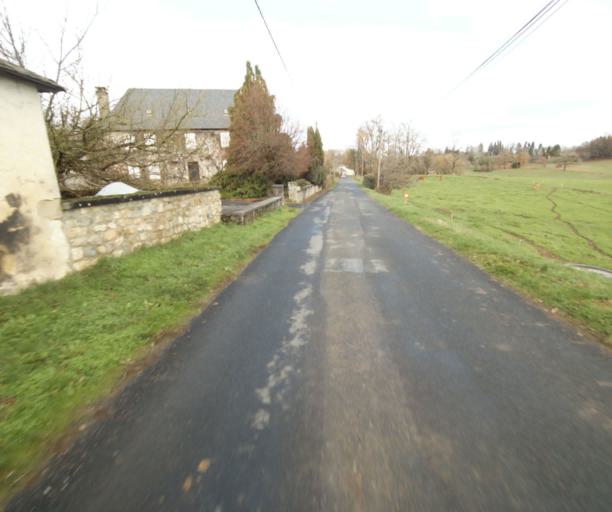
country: FR
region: Limousin
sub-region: Departement de la Correze
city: Sainte-Fereole
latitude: 45.2717
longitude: 1.6027
